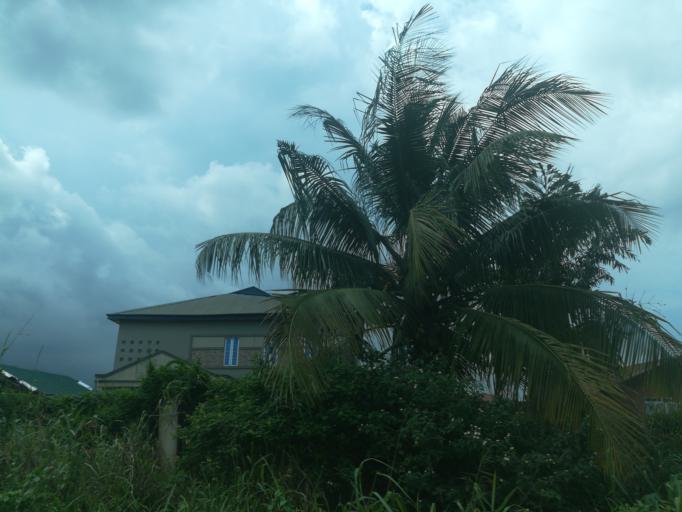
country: NG
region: Lagos
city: Ikorodu
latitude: 6.6456
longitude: 3.5588
